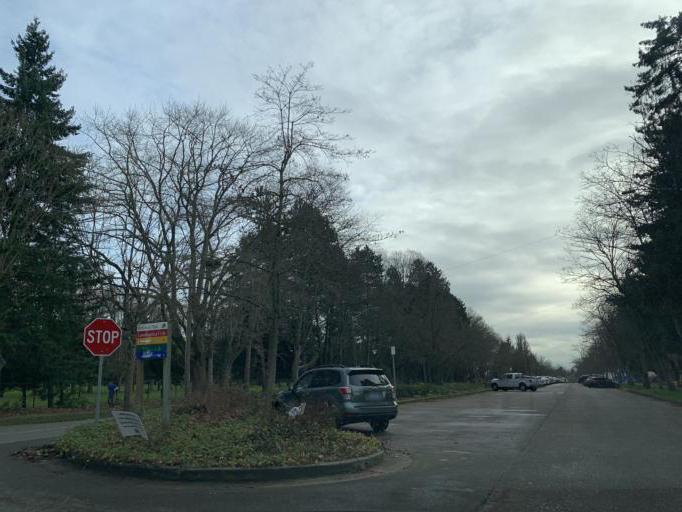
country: US
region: Washington
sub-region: King County
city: Seattle
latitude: 47.5668
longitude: -122.3069
